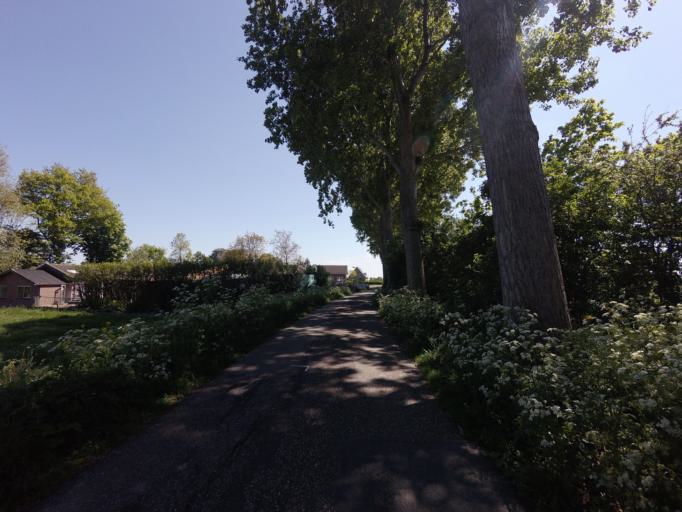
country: NL
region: Utrecht
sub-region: Gemeente De Ronde Venen
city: Mijdrecht
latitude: 52.2205
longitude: 4.8927
